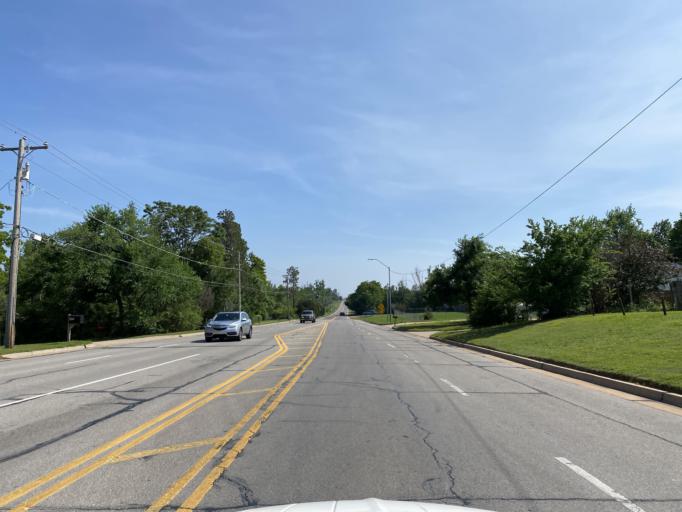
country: US
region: Oklahoma
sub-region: Oklahoma County
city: Nicoma Park
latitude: 35.4636
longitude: -97.3357
